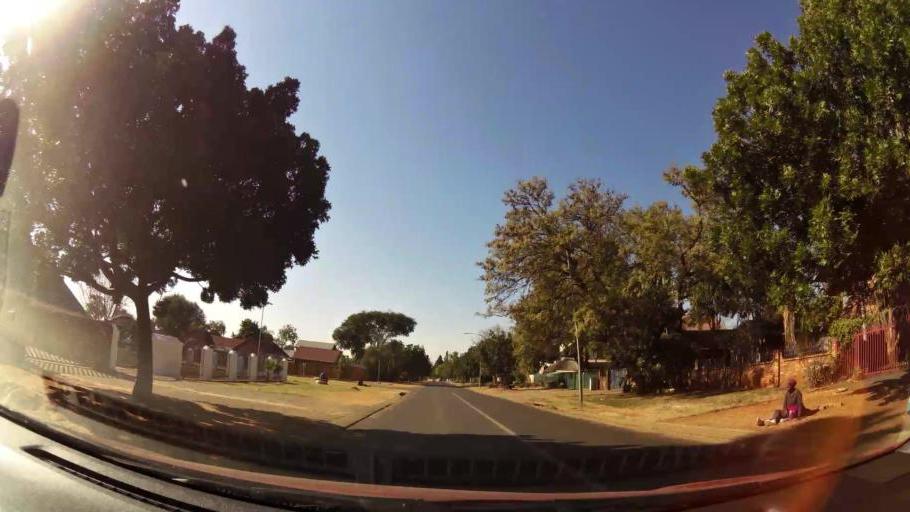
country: ZA
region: North-West
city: Ga-Rankuwa
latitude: -25.6500
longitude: 28.0949
